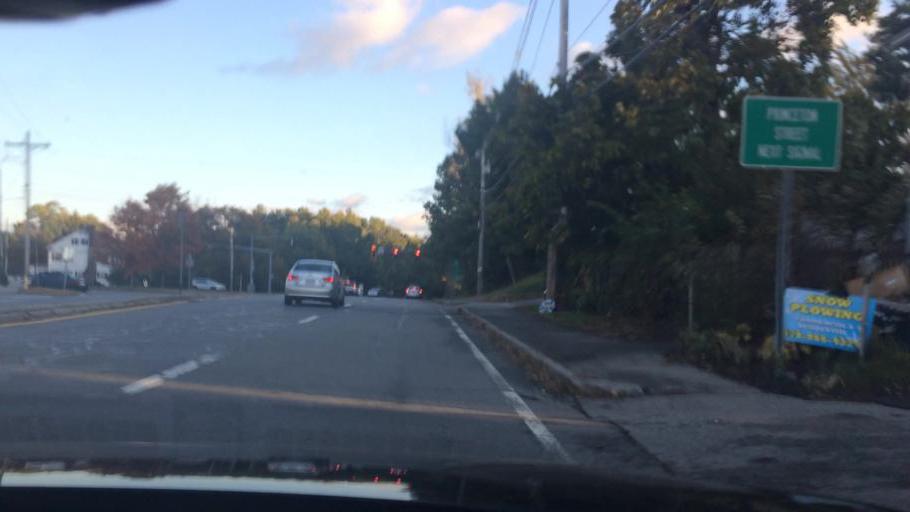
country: US
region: Massachusetts
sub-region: Middlesex County
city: Chelmsford
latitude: 42.6319
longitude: -71.3748
